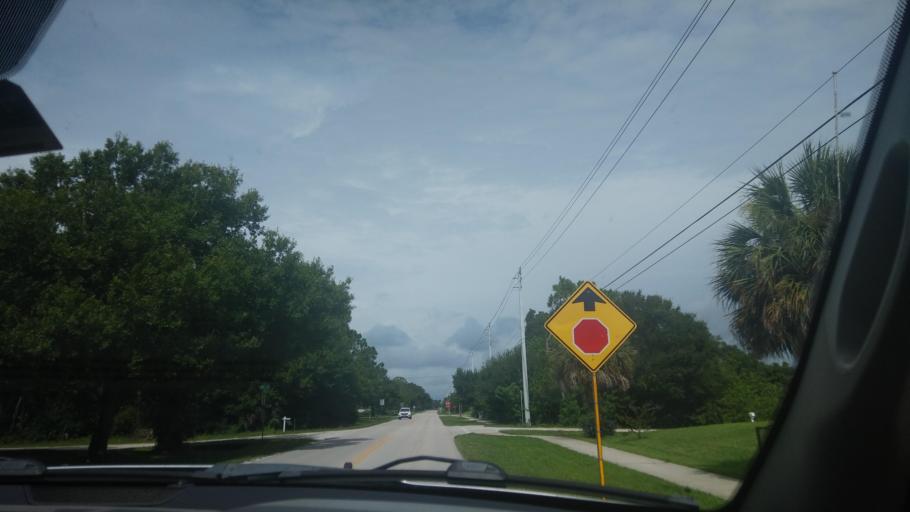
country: US
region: Florida
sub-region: Indian River County
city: Fellsmere
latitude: 27.7527
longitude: -80.5323
